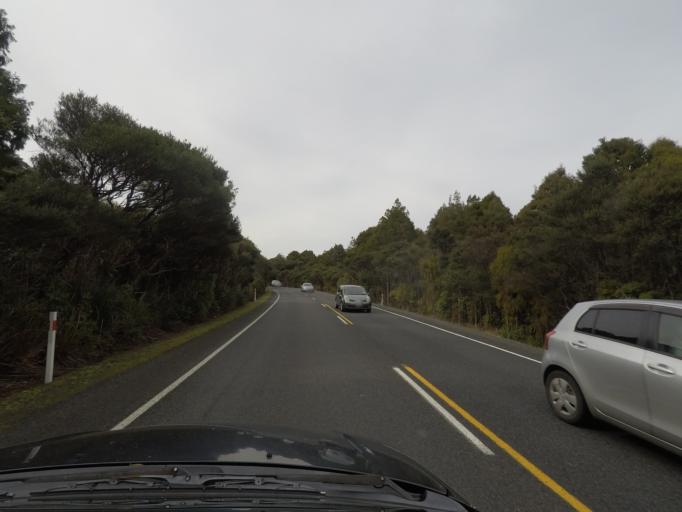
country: NZ
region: Auckland
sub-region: Auckland
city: Titirangi
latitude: -36.9451
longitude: 174.5284
